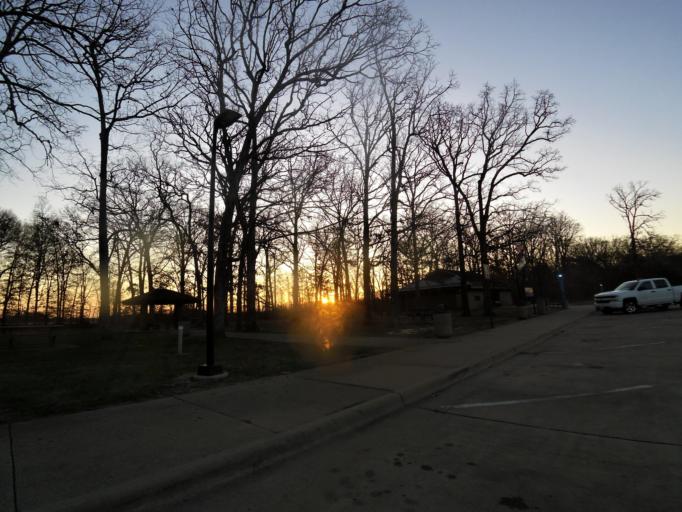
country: US
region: Illinois
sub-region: Marion County
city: Salem
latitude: 38.5967
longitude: -88.9642
